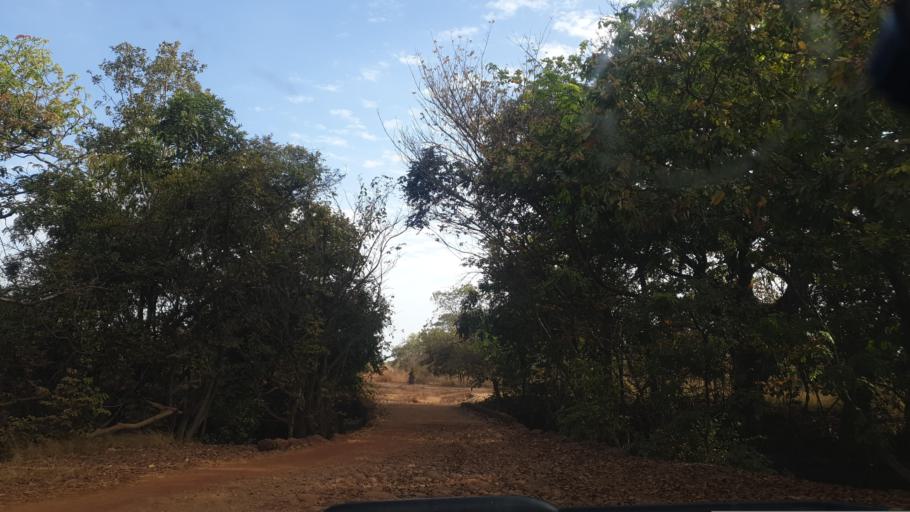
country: ML
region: Sikasso
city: Yanfolila
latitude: 11.2537
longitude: -8.1066
